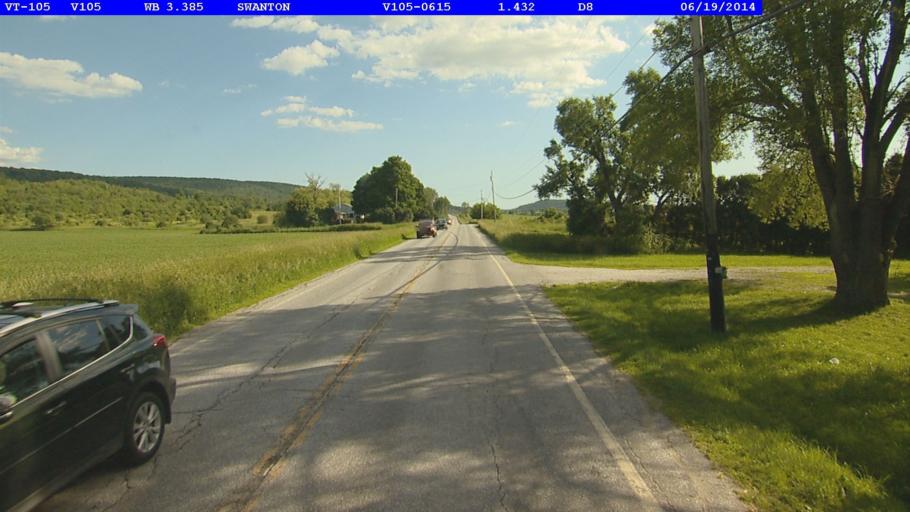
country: US
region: Vermont
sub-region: Franklin County
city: Saint Albans
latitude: 44.8533
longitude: -73.0353
